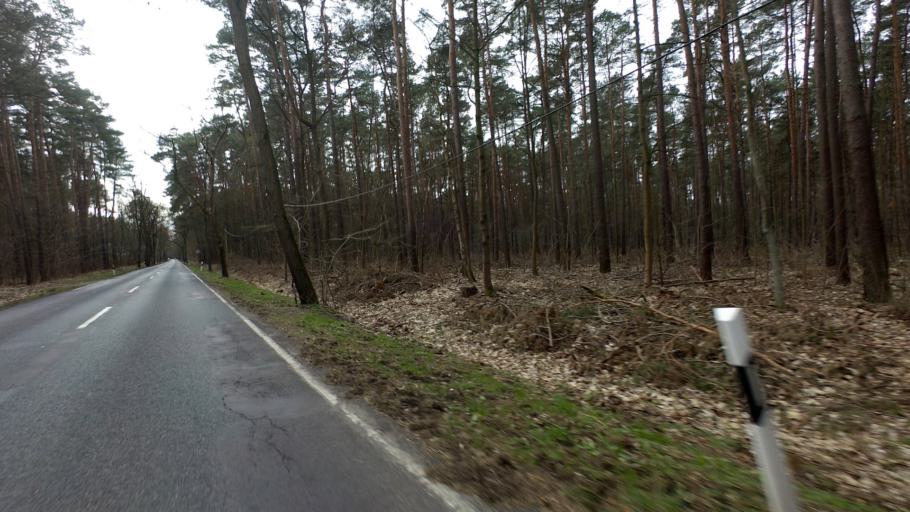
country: DE
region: Brandenburg
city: Wandlitz
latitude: 52.7426
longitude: 13.3717
